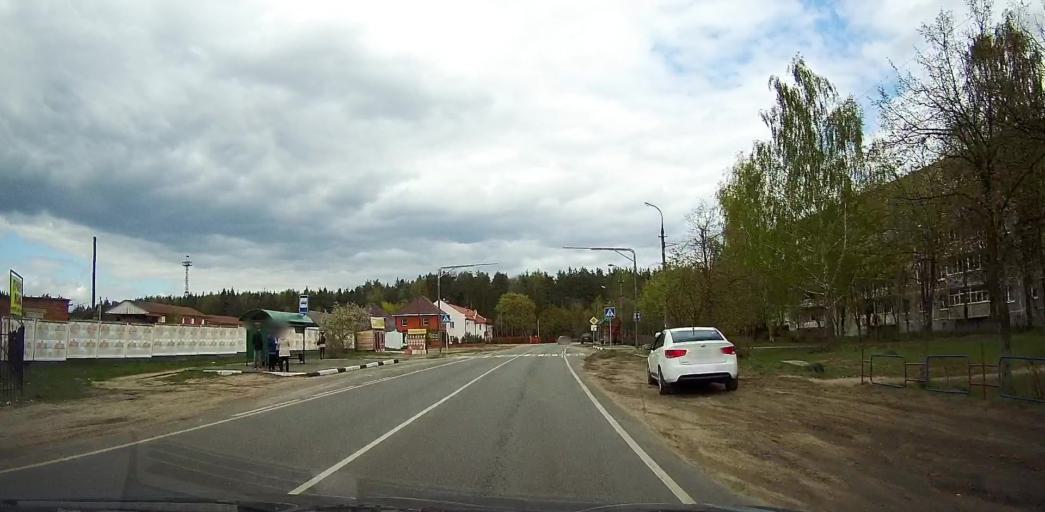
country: RU
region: Moskovskaya
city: Ashitkovo
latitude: 55.4375
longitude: 38.5793
